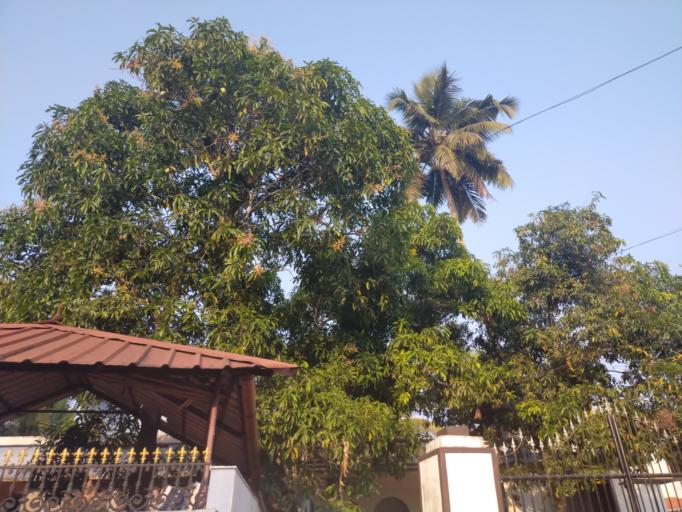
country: IN
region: Kerala
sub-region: Kottayam
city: Vaikam
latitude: 9.7561
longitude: 76.4980
